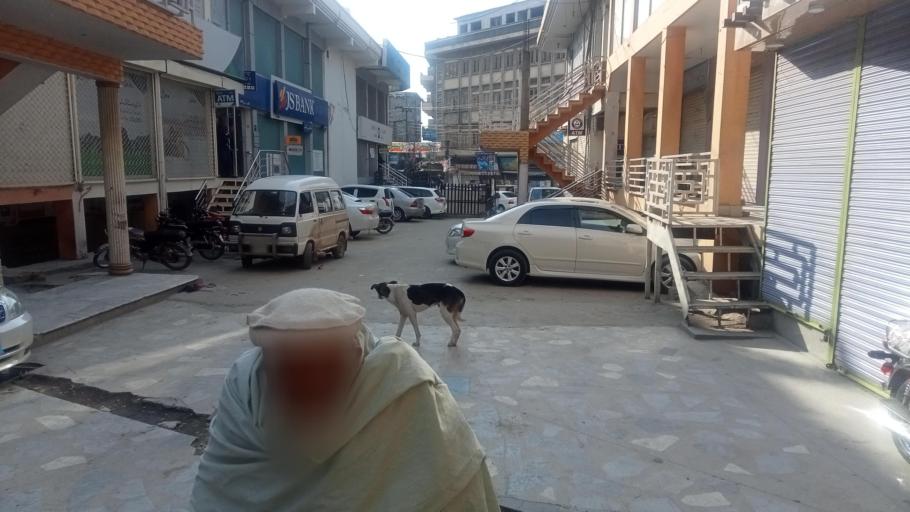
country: PK
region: Khyber Pakhtunkhwa
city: Mingora
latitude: 34.7771
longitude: 72.3590
